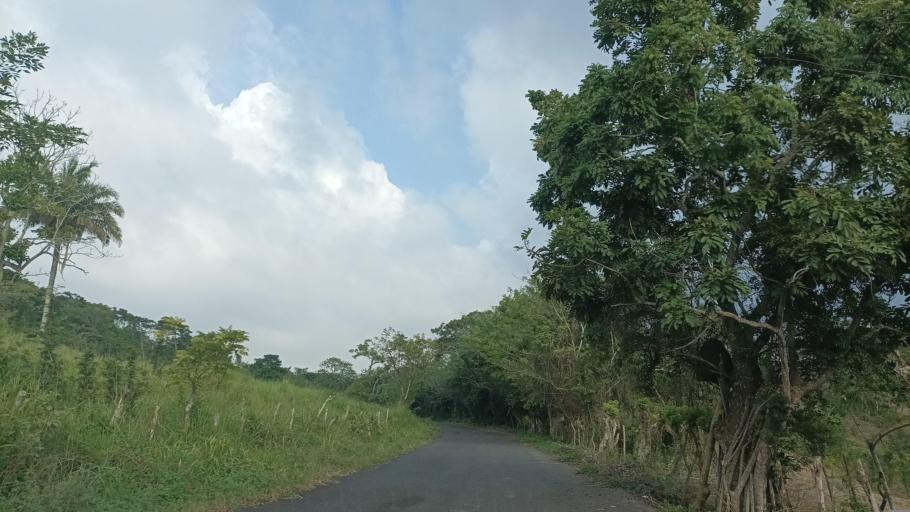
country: MX
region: Veracruz
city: Allende
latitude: 18.1183
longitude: -94.2893
